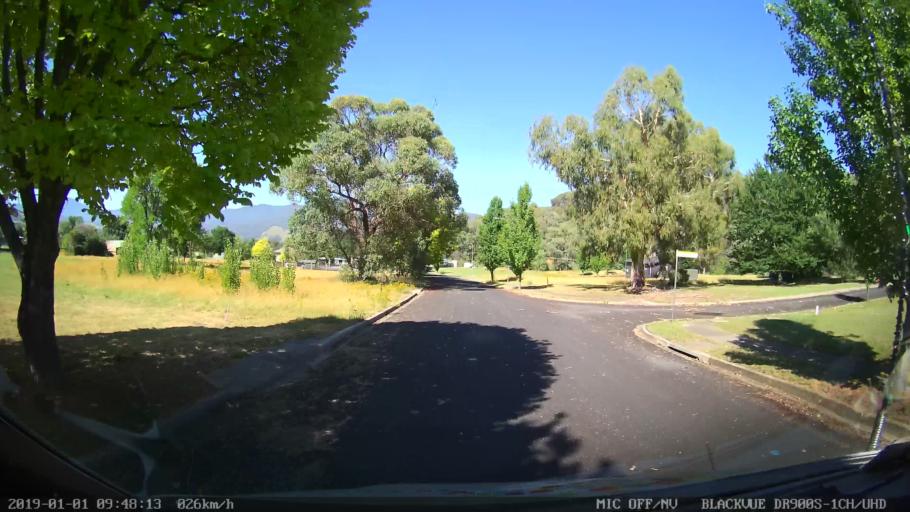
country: AU
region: New South Wales
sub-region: Snowy River
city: Jindabyne
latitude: -36.2112
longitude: 148.1333
